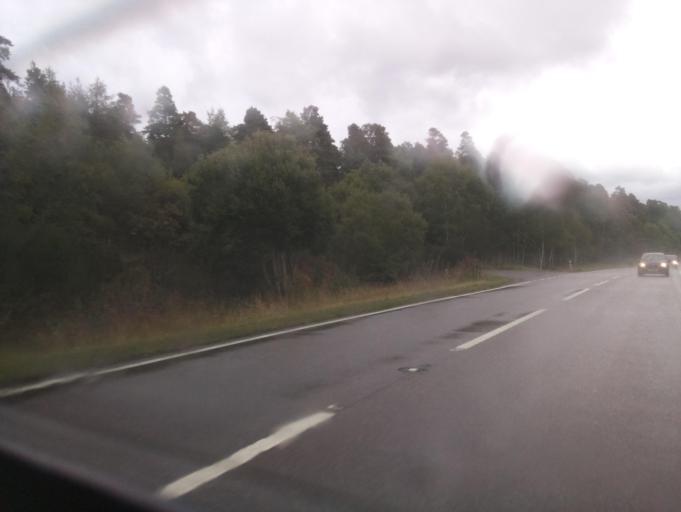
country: GB
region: Scotland
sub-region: Highland
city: Grantown on Spey
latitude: 57.2819
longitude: -3.6831
